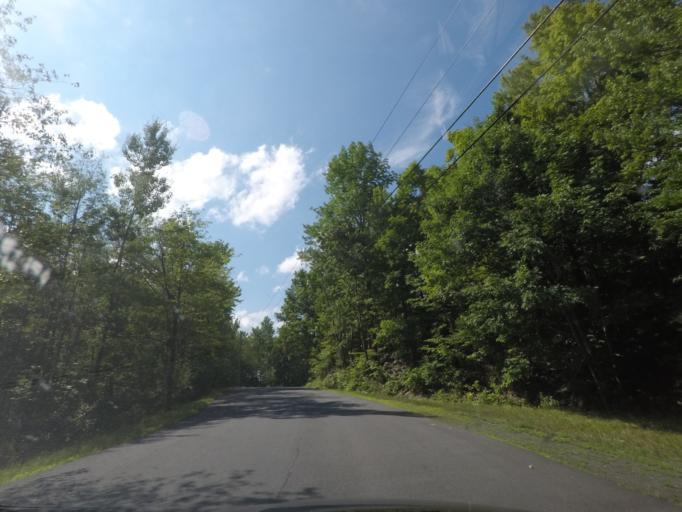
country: US
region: New York
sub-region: Rensselaer County
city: Averill Park
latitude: 42.6056
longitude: -73.5832
